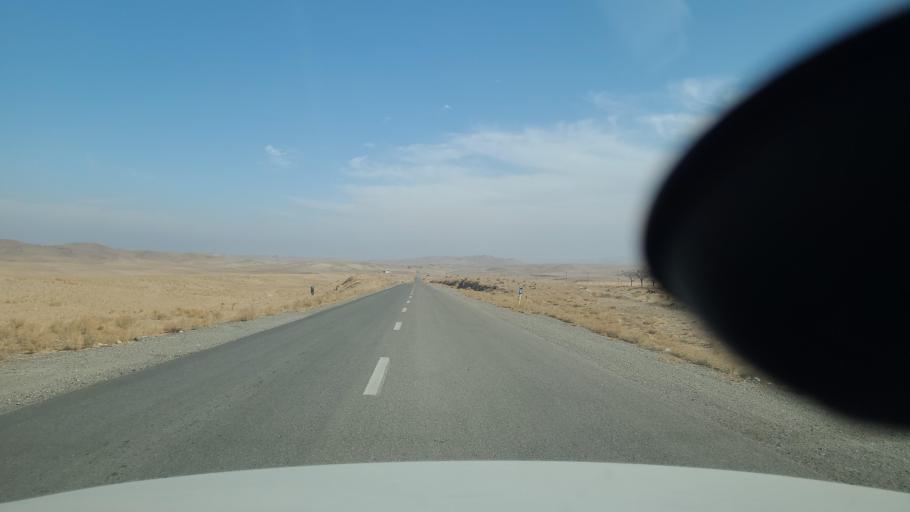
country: IR
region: Razavi Khorasan
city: Fariman
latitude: 35.5959
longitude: 59.7283
